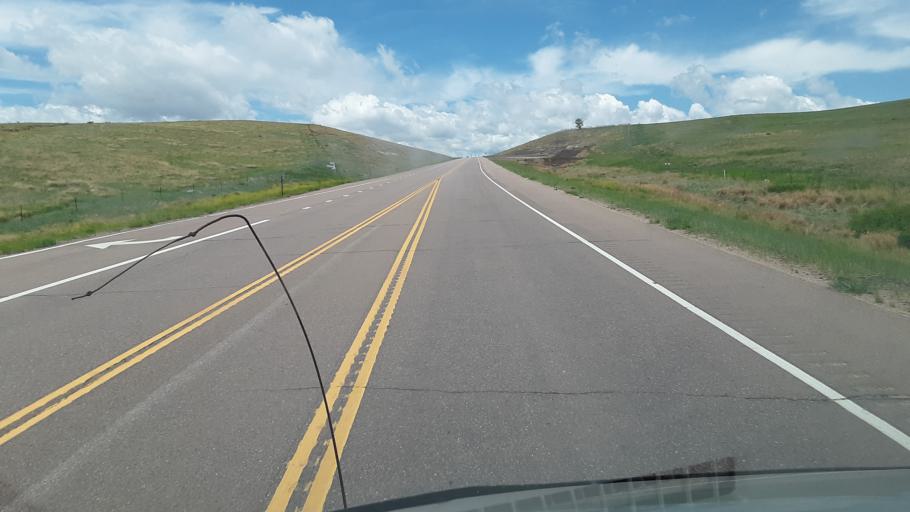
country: US
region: Colorado
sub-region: El Paso County
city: Cimarron Hills
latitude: 38.8397
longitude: -104.6732
